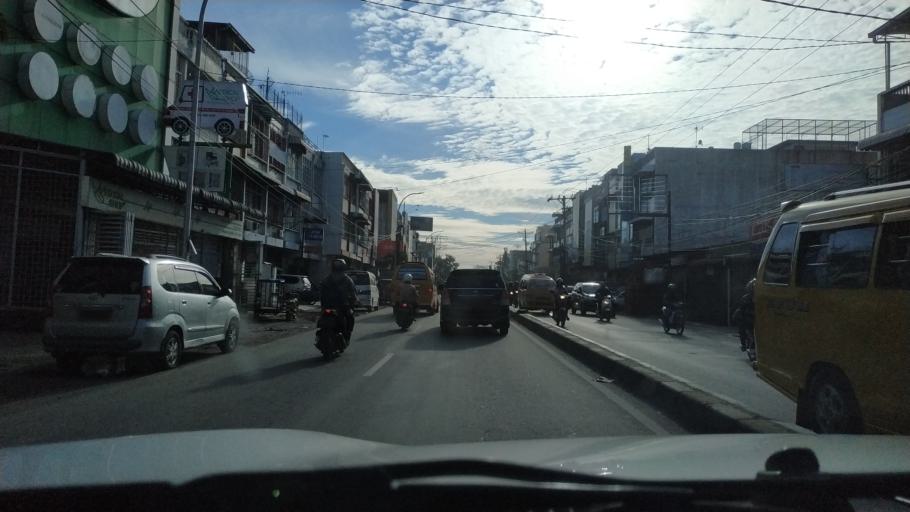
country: ID
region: North Sumatra
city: Medan
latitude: 3.5981
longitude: 98.7025
